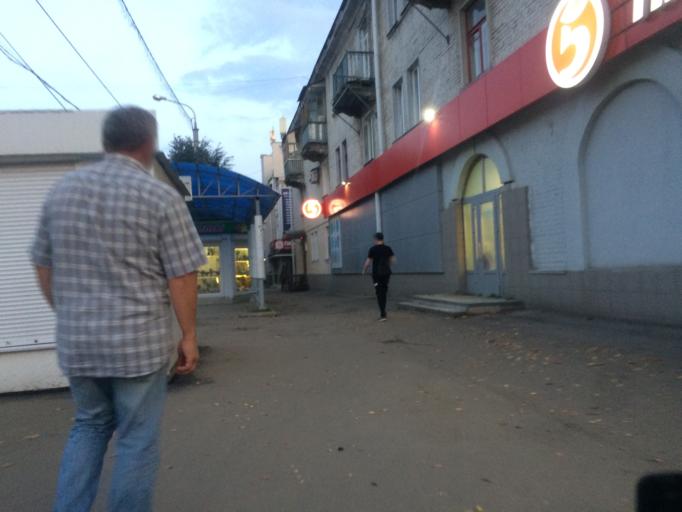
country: RU
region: Mariy-El
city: Yoshkar-Ola
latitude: 56.6367
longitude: 47.8735
